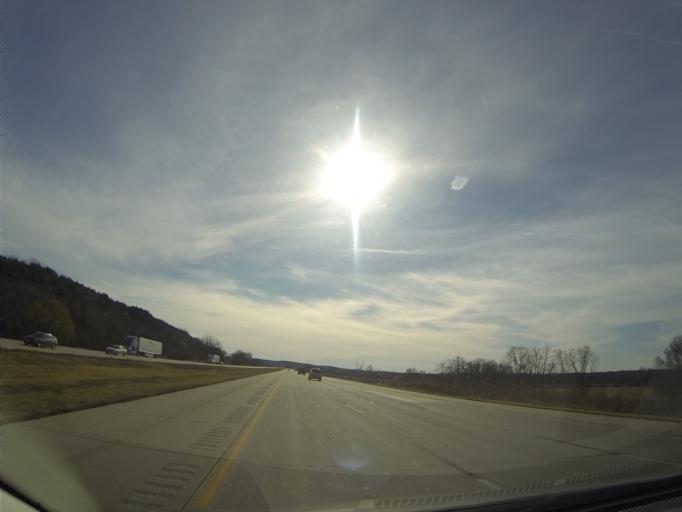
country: US
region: Nebraska
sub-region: Saunders County
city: Ashland
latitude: 41.0485
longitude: -96.2959
